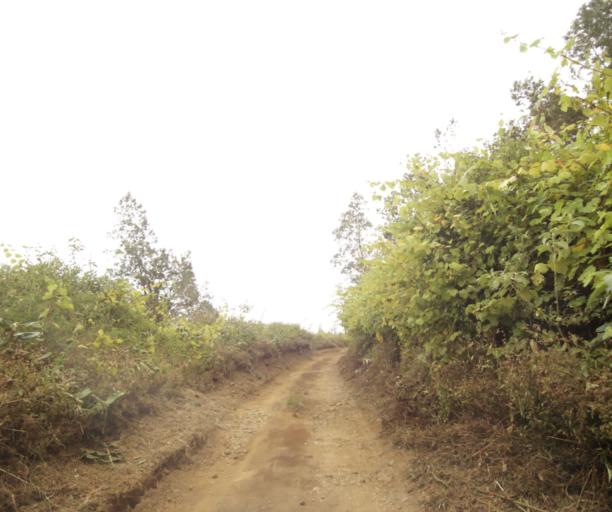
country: RE
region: Reunion
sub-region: Reunion
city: La Possession
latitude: -21.0133
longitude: 55.3582
